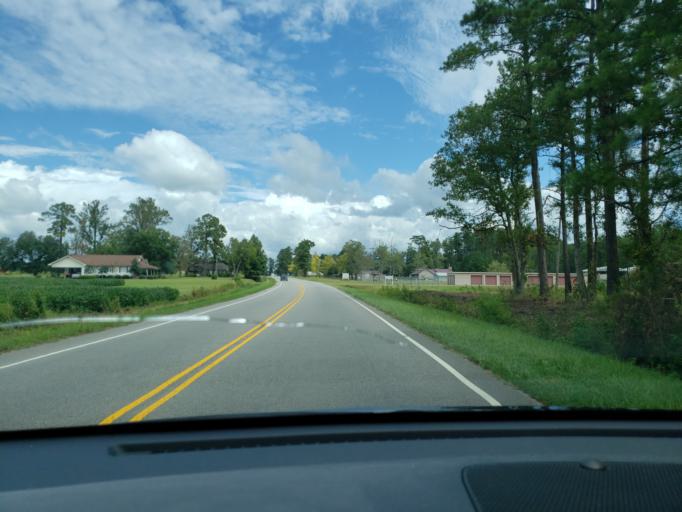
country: US
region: North Carolina
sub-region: Columbus County
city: Brunswick
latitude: 34.1955
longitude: -78.7680
